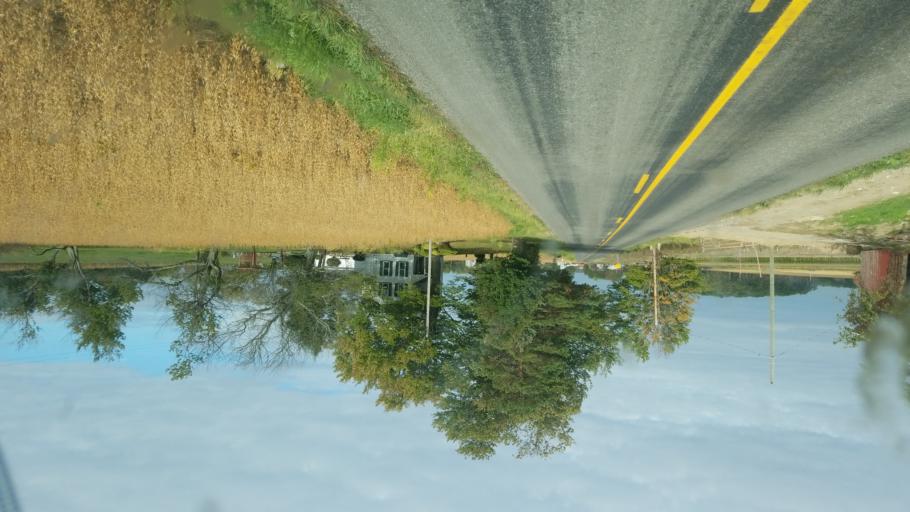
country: US
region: Pennsylvania
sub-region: Mercer County
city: Reynolds Heights
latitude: 41.3439
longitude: -80.2795
